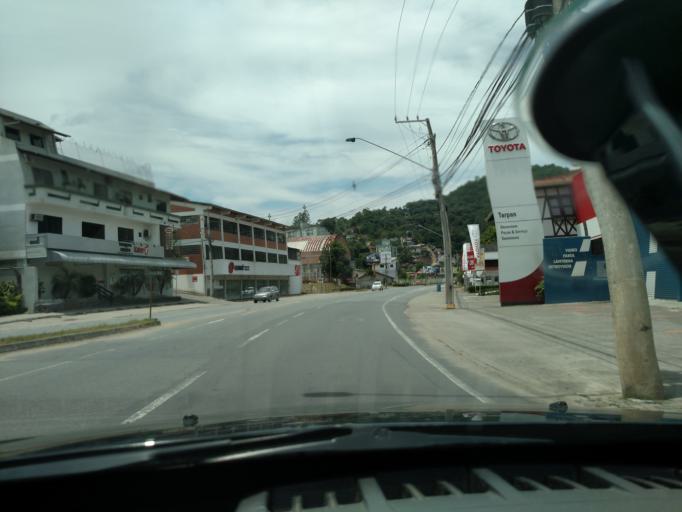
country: BR
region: Santa Catarina
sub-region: Blumenau
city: Blumenau
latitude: -26.8934
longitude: -49.0631
